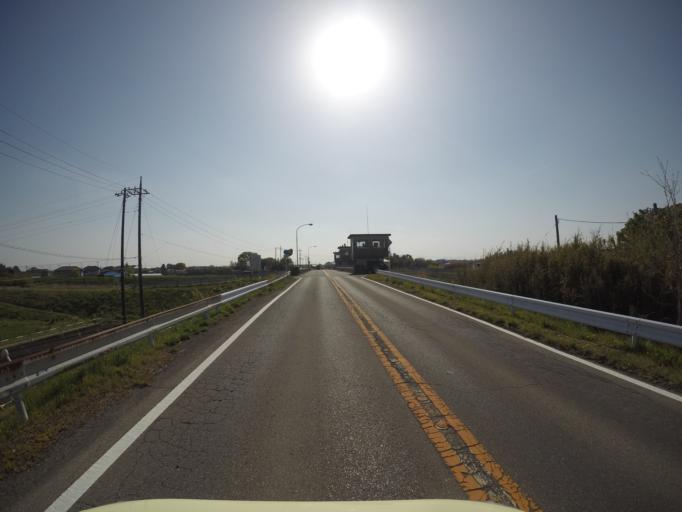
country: JP
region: Ibaraki
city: Yuki
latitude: 36.3616
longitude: 139.9030
